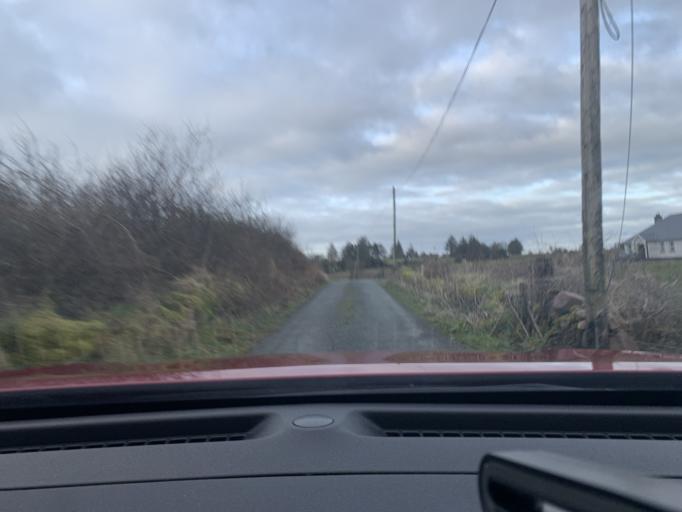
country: IE
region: Connaught
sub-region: Roscommon
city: Ballaghaderreen
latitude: 53.9718
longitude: -8.5592
